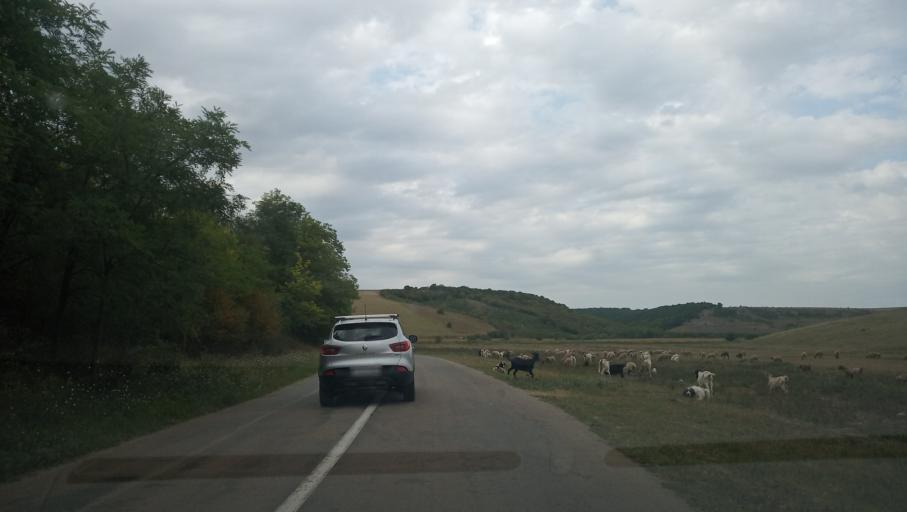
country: RO
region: Constanta
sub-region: Comuna Dumbraveni
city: Dumbraveni
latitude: 44.0061
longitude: 28.0013
